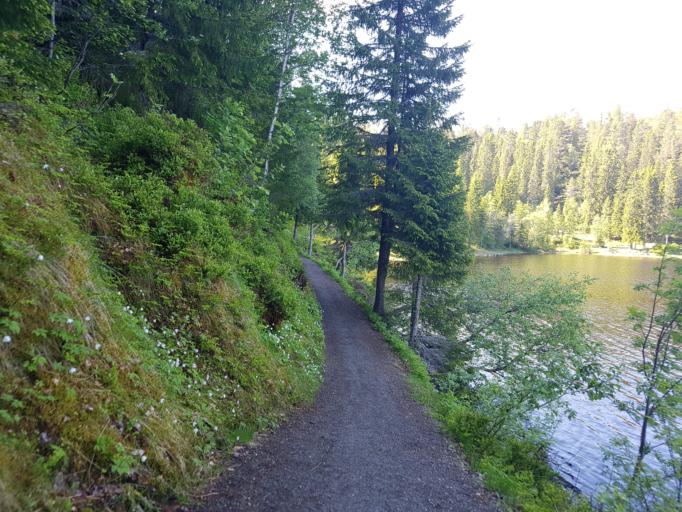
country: NO
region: Sor-Trondelag
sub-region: Trondheim
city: Trondheim
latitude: 63.4230
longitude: 10.2784
